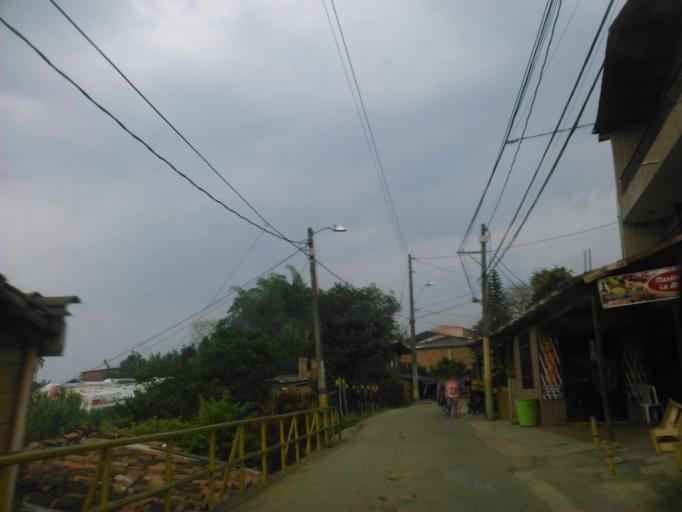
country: CO
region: Antioquia
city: La Estrella
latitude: 6.1381
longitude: -75.6410
